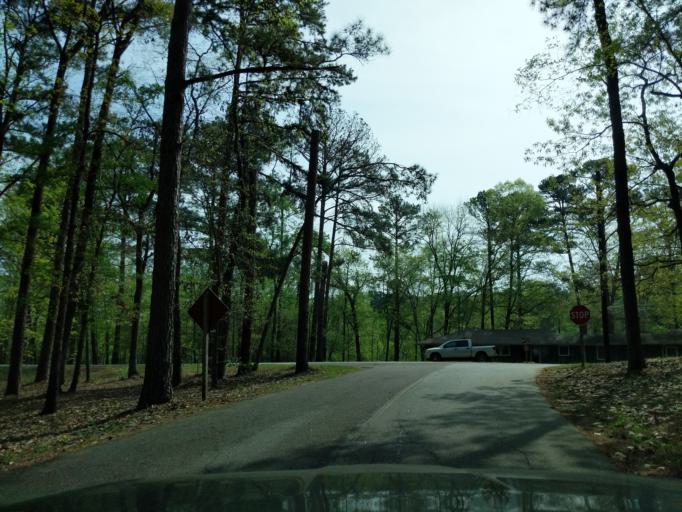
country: US
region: Georgia
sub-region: Lincoln County
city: Lincolnton
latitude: 33.8554
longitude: -82.4081
